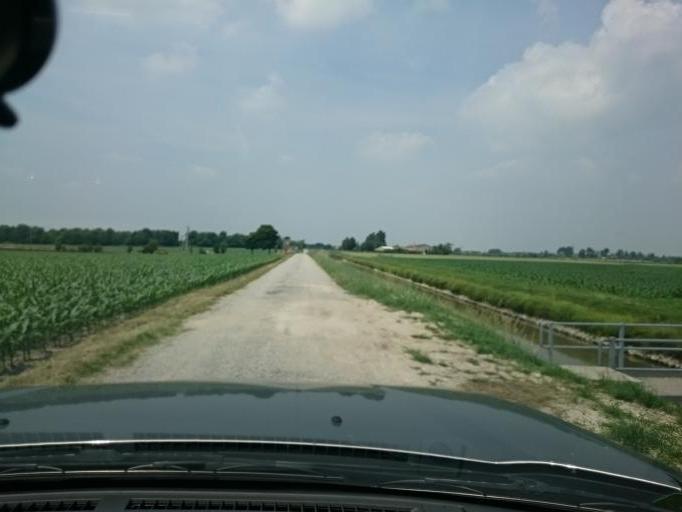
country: IT
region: Veneto
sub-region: Provincia di Padova
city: Vallonga
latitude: 45.2514
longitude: 12.0832
